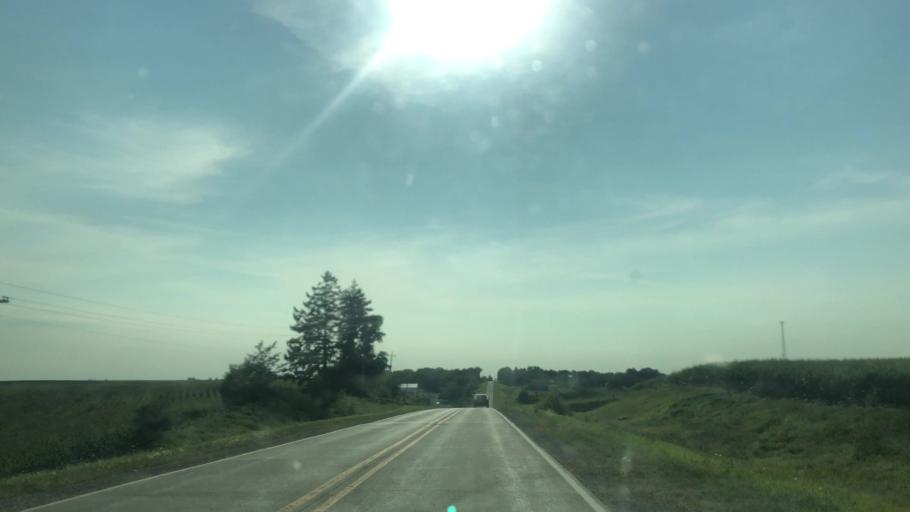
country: US
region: Iowa
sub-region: Marshall County
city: Marshalltown
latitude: 42.0488
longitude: -92.9961
